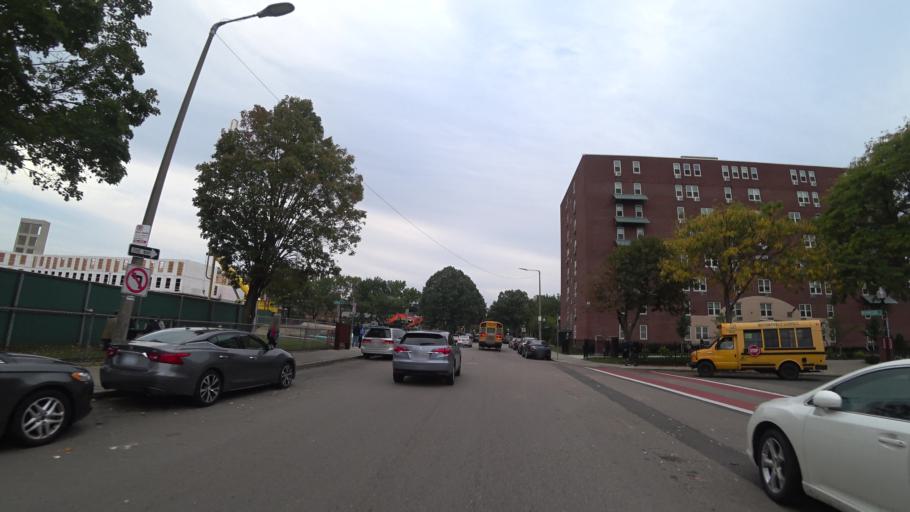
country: US
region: Massachusetts
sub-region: Suffolk County
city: South Boston
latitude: 42.3347
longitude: -71.0818
